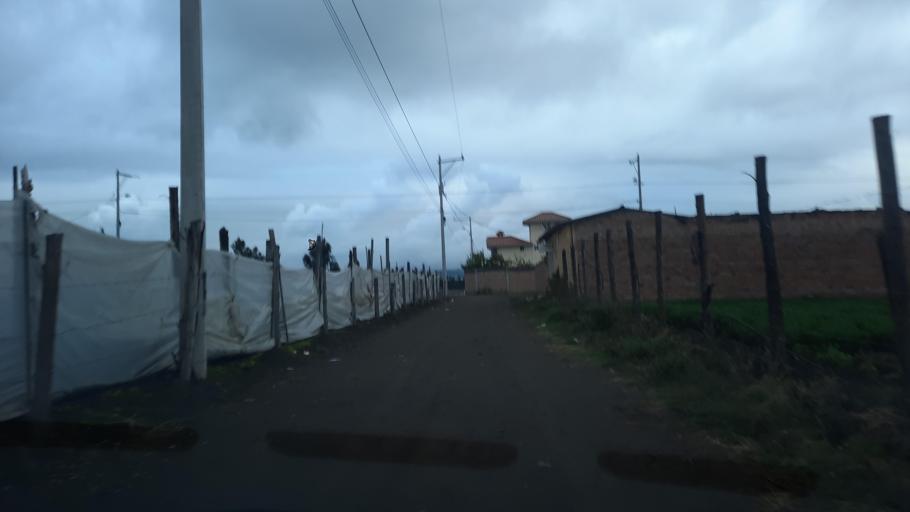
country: EC
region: Chimborazo
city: Riobamba
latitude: -1.6862
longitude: -78.6618
